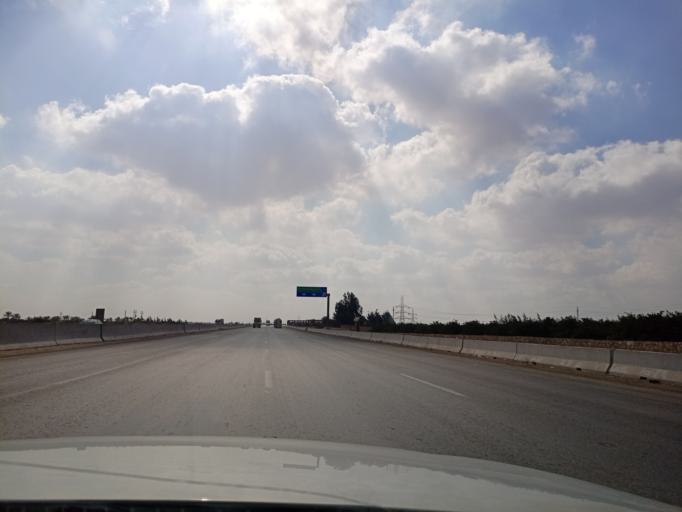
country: EG
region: Eastern Province
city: Bilbays
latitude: 30.3494
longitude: 31.5539
